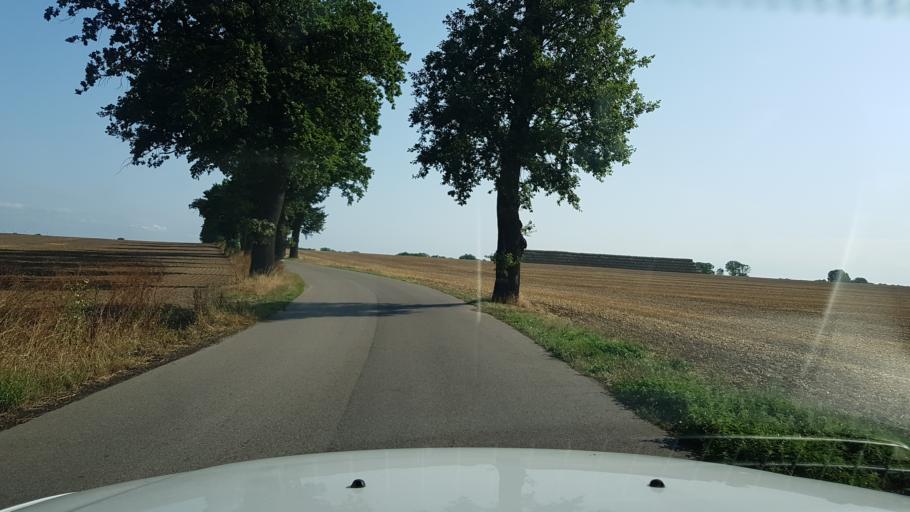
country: PL
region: West Pomeranian Voivodeship
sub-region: Powiat stargardzki
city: Stargard Szczecinski
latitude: 53.2635
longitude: 15.1141
